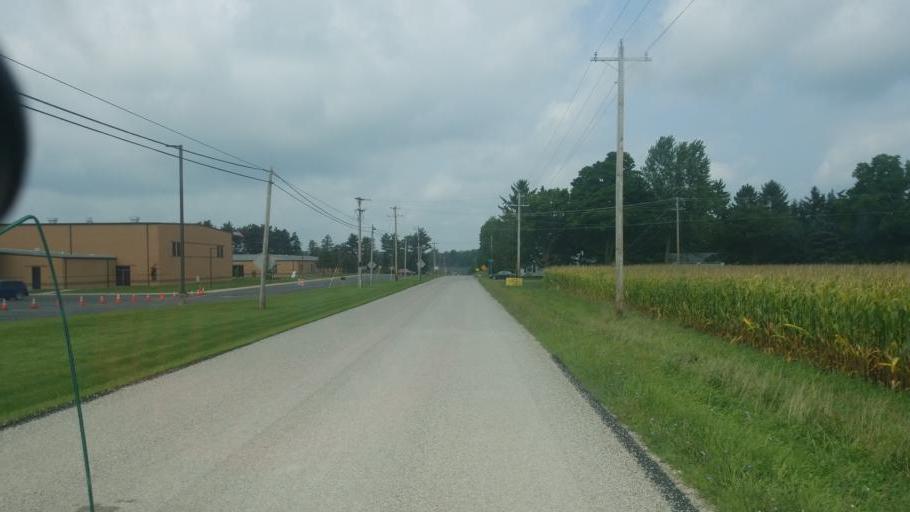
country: US
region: Ohio
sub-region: Huron County
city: Greenwich
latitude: 41.0474
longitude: -82.5176
